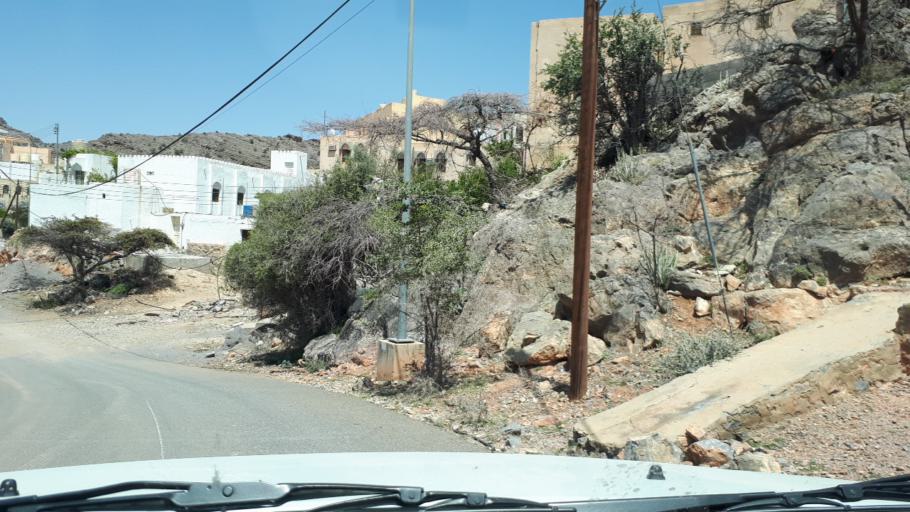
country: OM
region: Muhafazat ad Dakhiliyah
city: Izki
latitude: 23.0923
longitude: 57.7322
